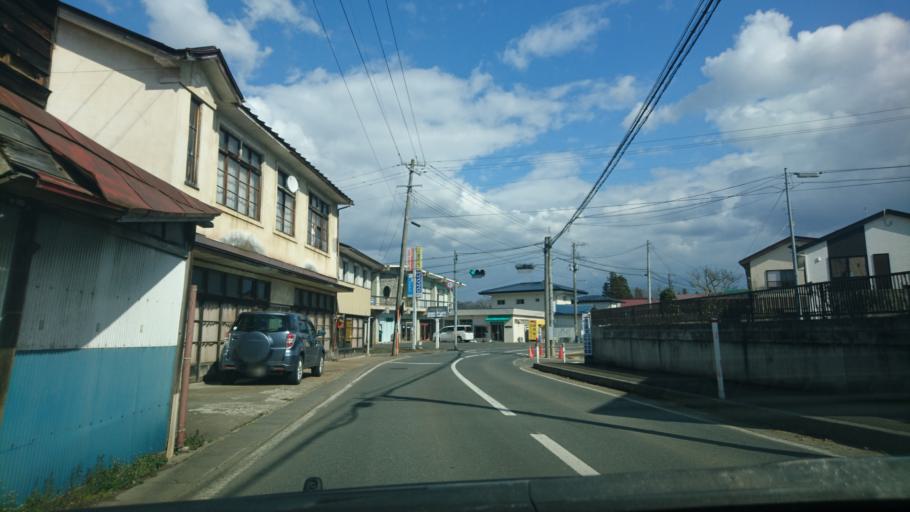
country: JP
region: Iwate
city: Kitakami
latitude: 39.2958
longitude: 141.2034
